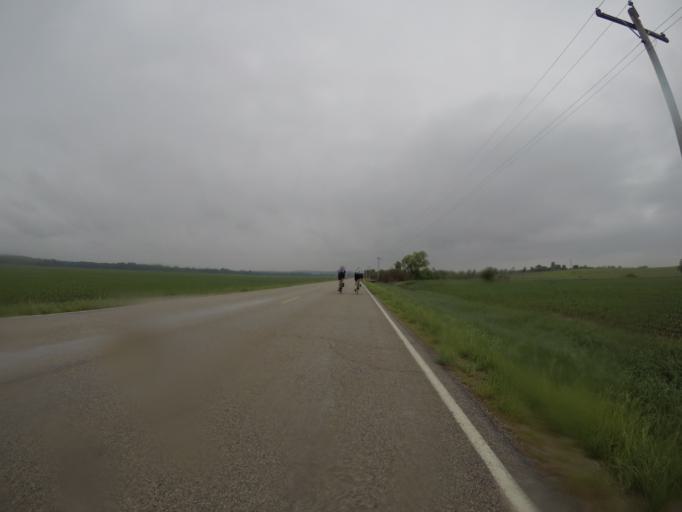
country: US
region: Kansas
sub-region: Pottawatomie County
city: Wamego
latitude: 39.3160
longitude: -96.2215
